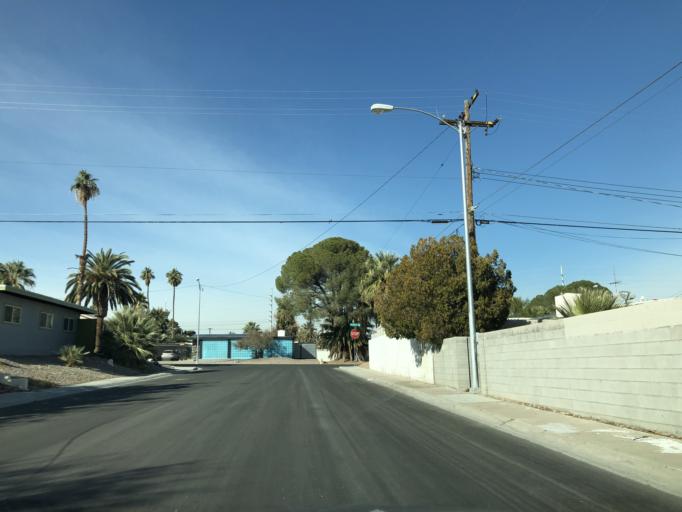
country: US
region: Nevada
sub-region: Clark County
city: Winchester
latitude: 36.1280
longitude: -115.1308
